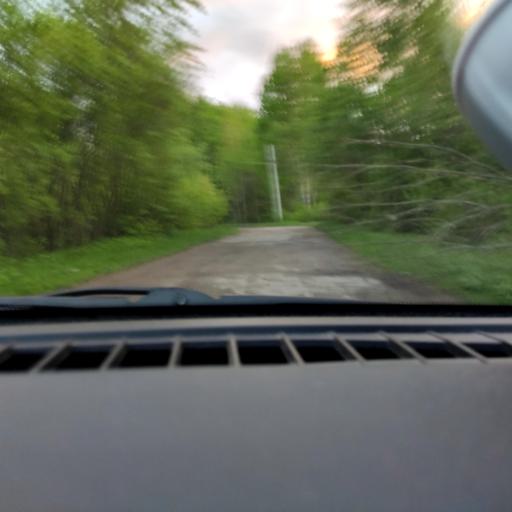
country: RU
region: Perm
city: Perm
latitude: 58.0818
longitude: 56.3838
